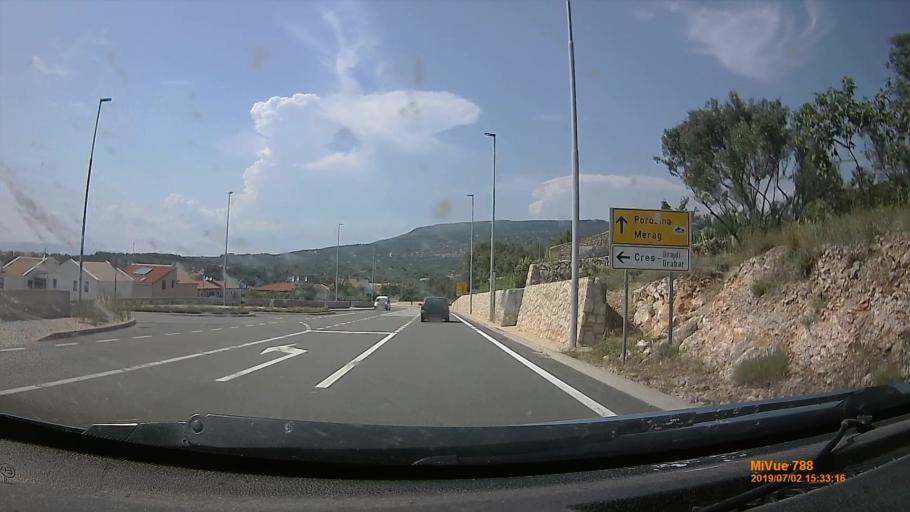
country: HR
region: Primorsko-Goranska
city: Cres
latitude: 44.9582
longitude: 14.4154
